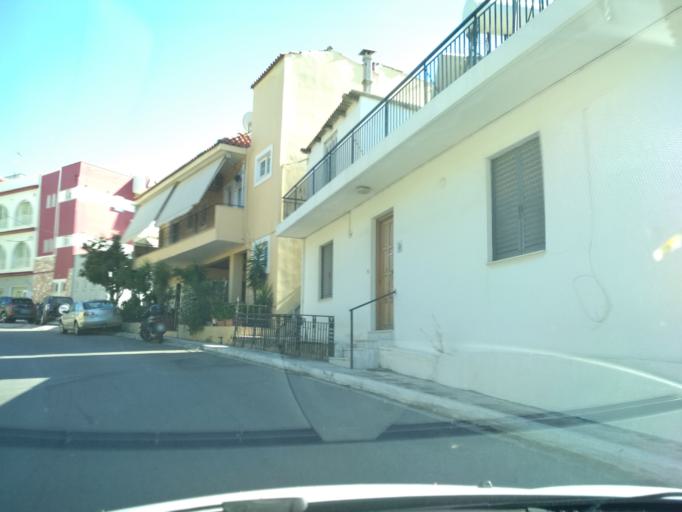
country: GR
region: Central Greece
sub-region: Nomos Evvoias
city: Oreoi
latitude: 38.8534
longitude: 23.0521
